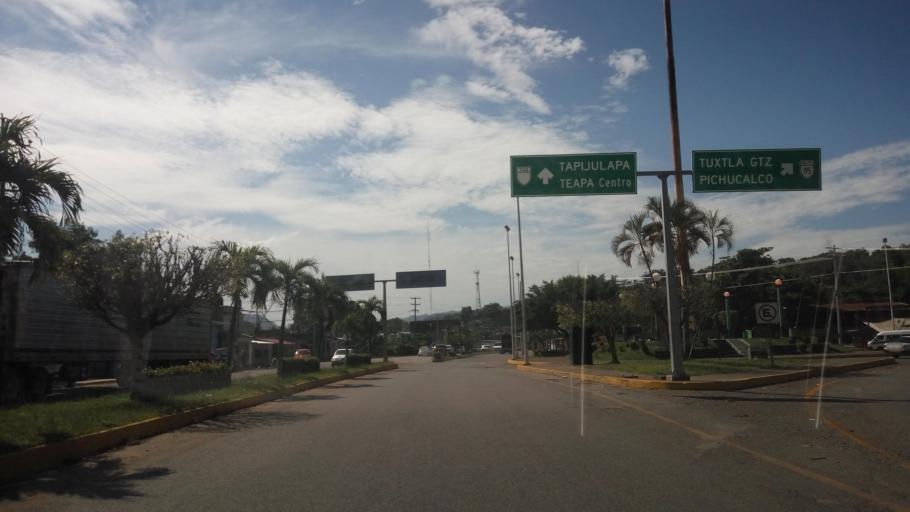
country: MX
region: Tabasco
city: Teapa
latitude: 17.5699
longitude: -92.9557
